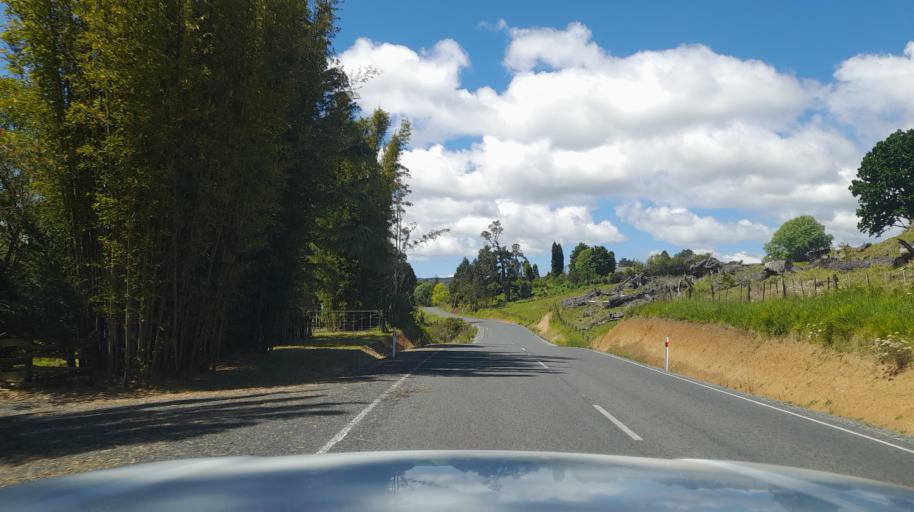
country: NZ
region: Northland
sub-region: Far North District
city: Taipa
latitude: -35.0962
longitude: 173.4936
